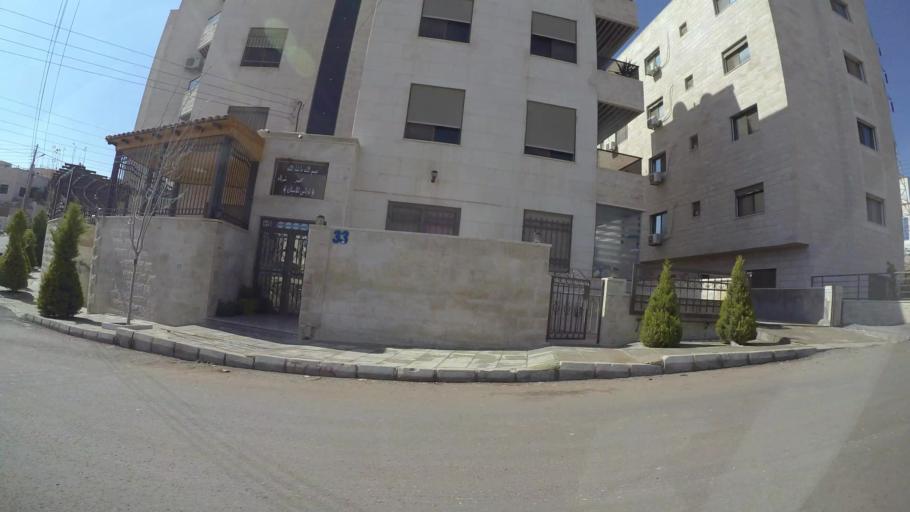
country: JO
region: Amman
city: Al Bunayyat ash Shamaliyah
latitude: 31.8901
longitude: 35.8978
